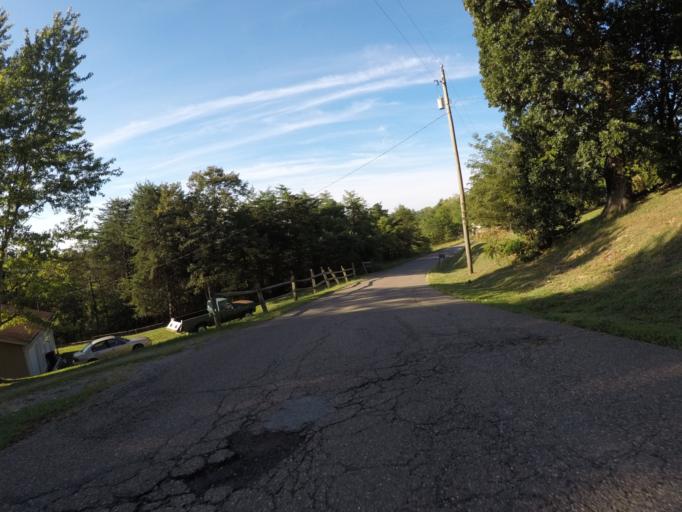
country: US
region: Ohio
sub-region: Lawrence County
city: Coal Grove
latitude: 38.5925
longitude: -82.5477
